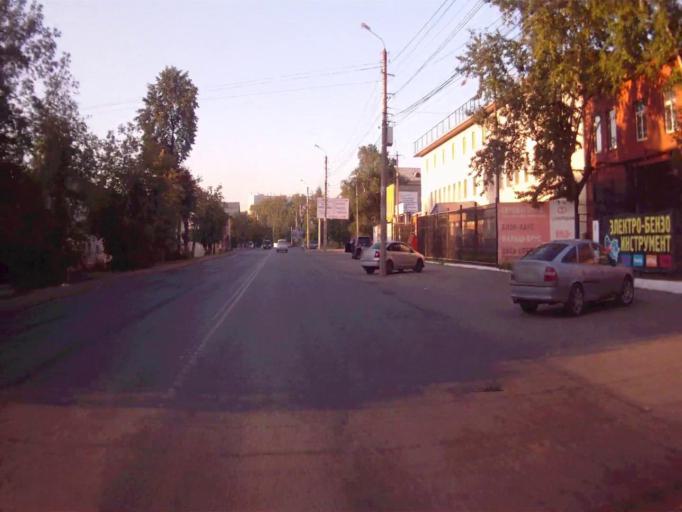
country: RU
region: Chelyabinsk
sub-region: Gorod Chelyabinsk
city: Chelyabinsk
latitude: 55.1658
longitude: 61.4346
